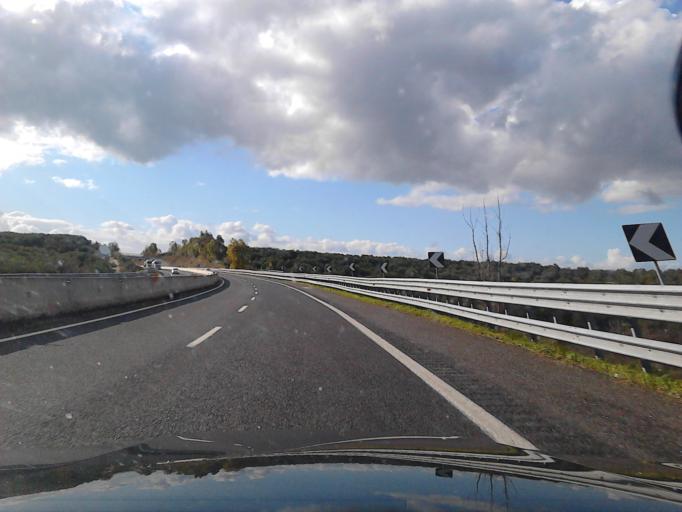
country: IT
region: Apulia
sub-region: Provincia di Barletta - Andria - Trani
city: Andria
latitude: 41.2624
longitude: 16.2488
